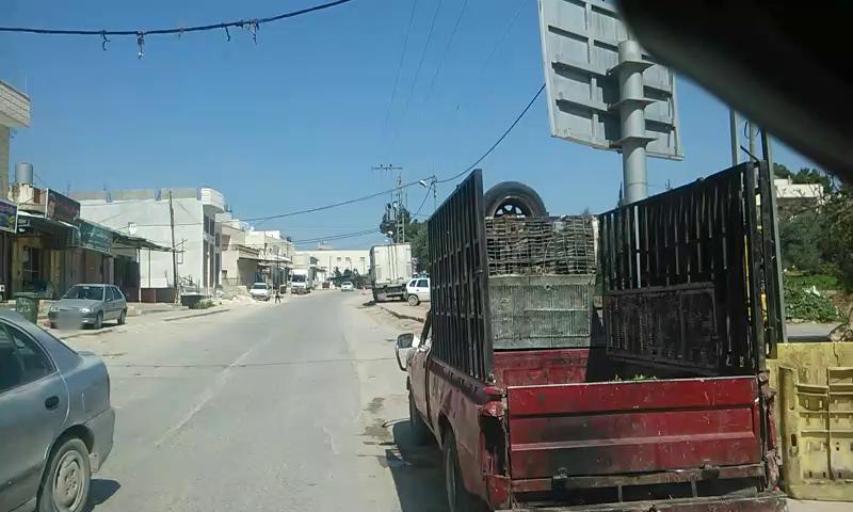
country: PS
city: Dayr Samit
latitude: 31.5197
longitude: 34.9763
